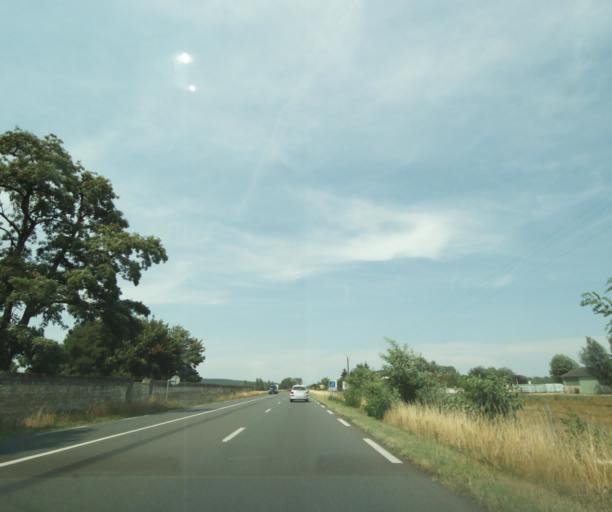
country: FR
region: Poitou-Charentes
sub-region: Departement de la Vienne
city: Antran
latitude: 46.8530
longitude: 0.5519
